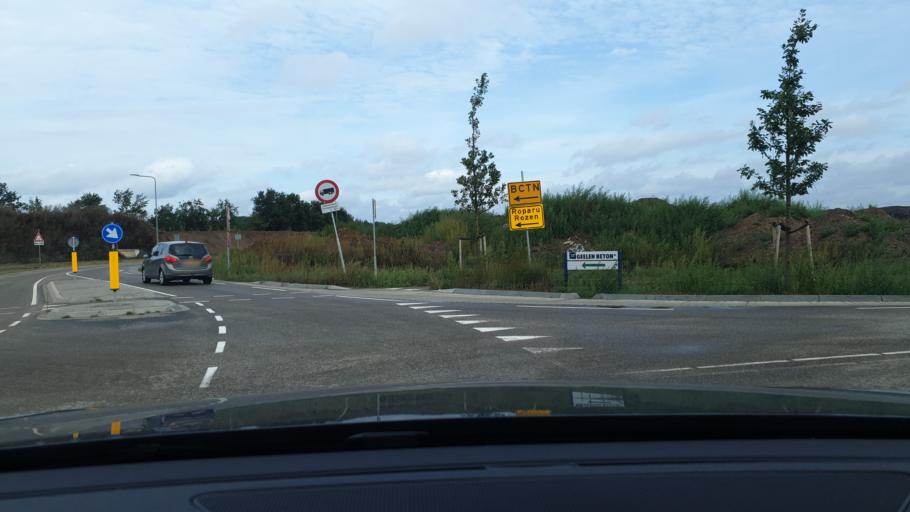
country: NL
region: Limburg
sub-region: Gemeente Bergen
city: Wellerlooi
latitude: 51.5404
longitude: 6.0711
